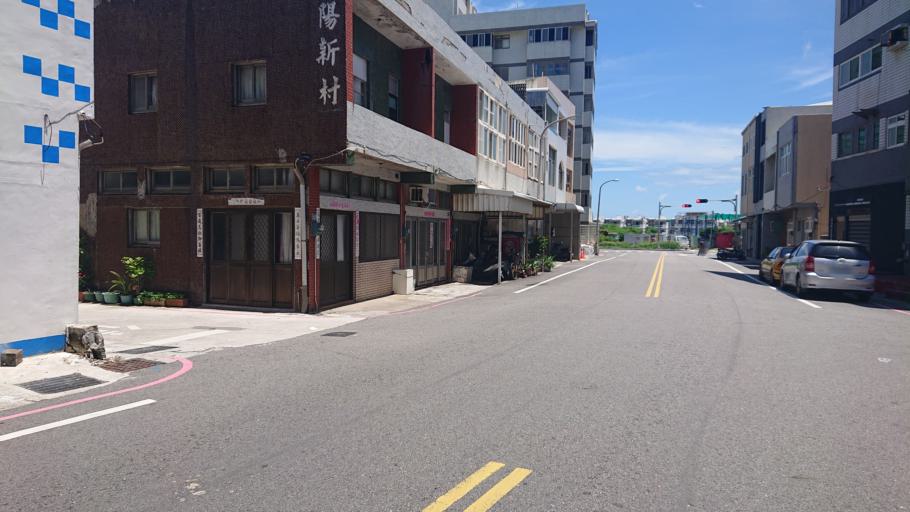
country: TW
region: Taiwan
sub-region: Penghu
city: Ma-kung
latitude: 23.5754
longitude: 119.5780
